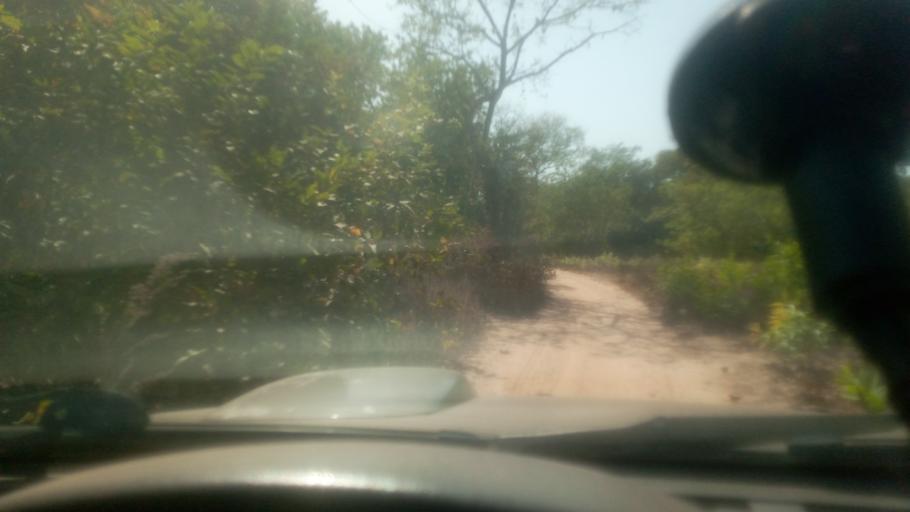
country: GW
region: Oio
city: Farim
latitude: 12.4535
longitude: -15.4183
